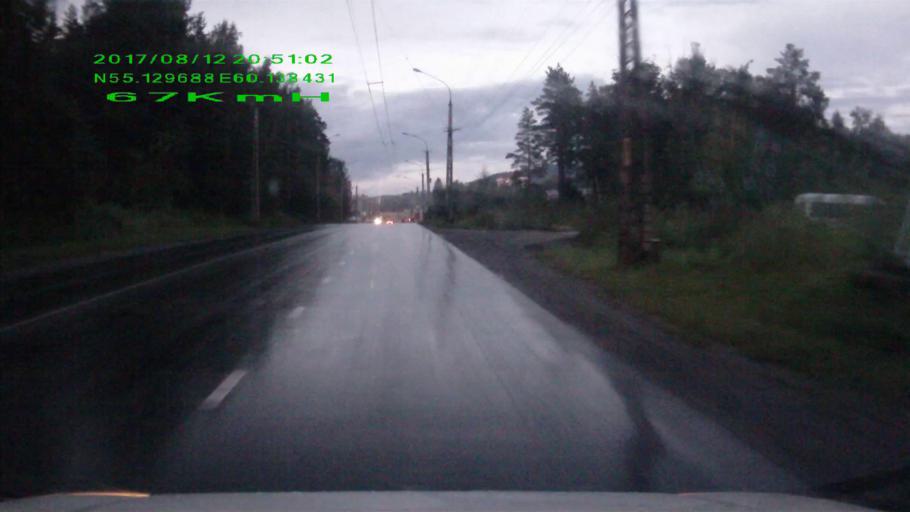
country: RU
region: Chelyabinsk
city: Turgoyak
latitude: 55.1298
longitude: 60.1387
